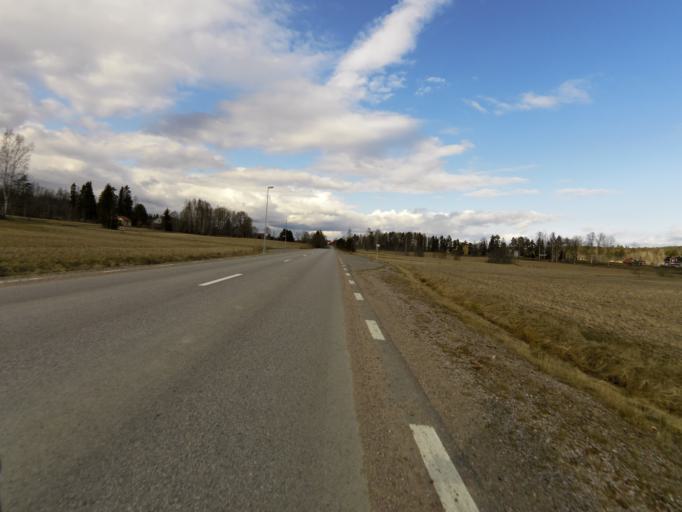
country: SE
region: Dalarna
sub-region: Avesta Kommun
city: Horndal
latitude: 60.4563
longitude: 16.4545
